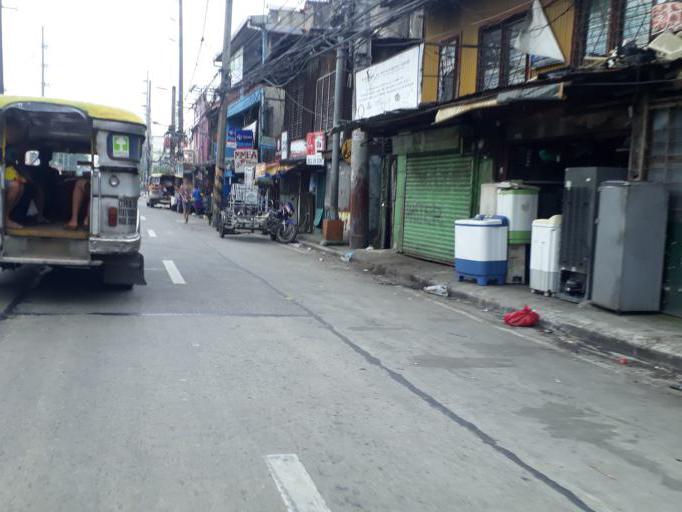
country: PH
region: Metro Manila
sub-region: Caloocan City
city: Niugan
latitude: 14.6584
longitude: 120.9686
